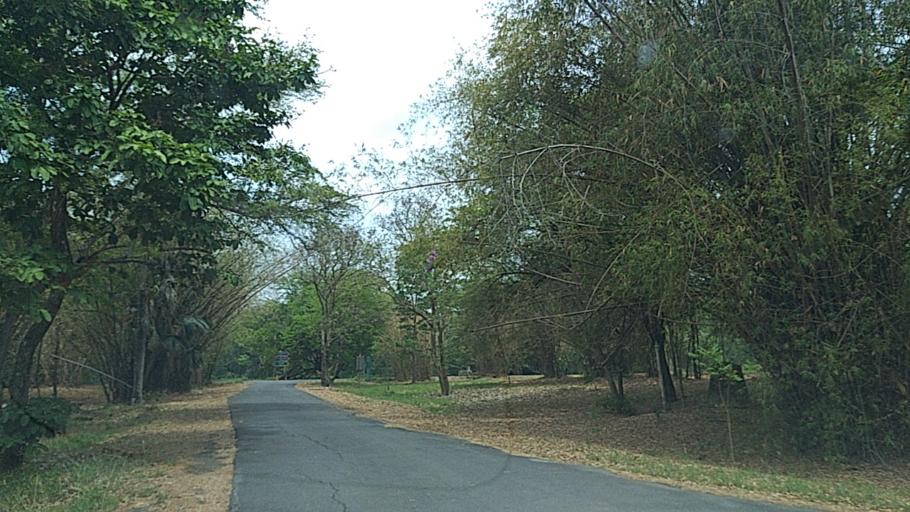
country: TH
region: Nakhon Pathom
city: Salaya
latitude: 13.7833
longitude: 100.3132
